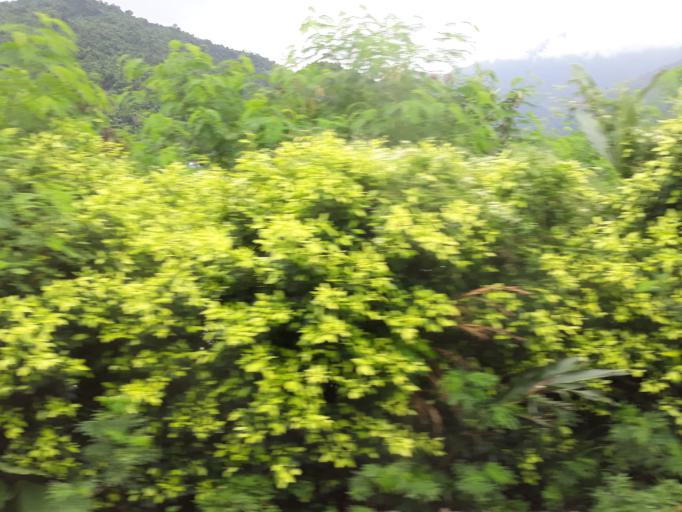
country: TW
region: Taiwan
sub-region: Yilan
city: Yilan
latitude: 24.4390
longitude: 121.7807
